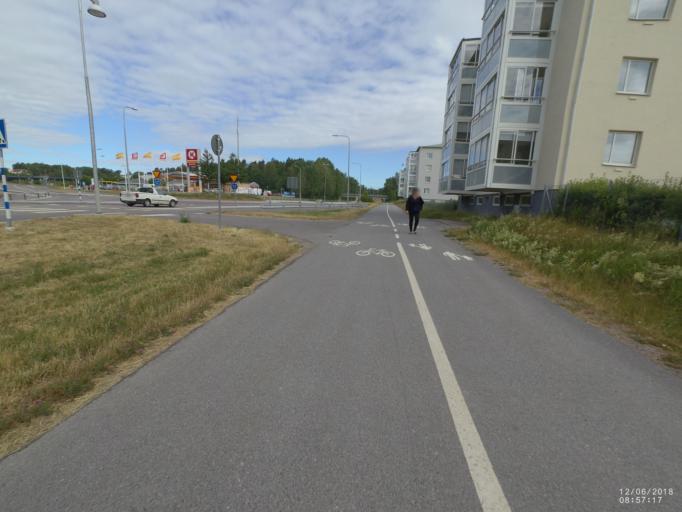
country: SE
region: Soedermanland
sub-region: Nykopings Kommun
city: Nykoping
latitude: 58.7569
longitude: 17.0344
